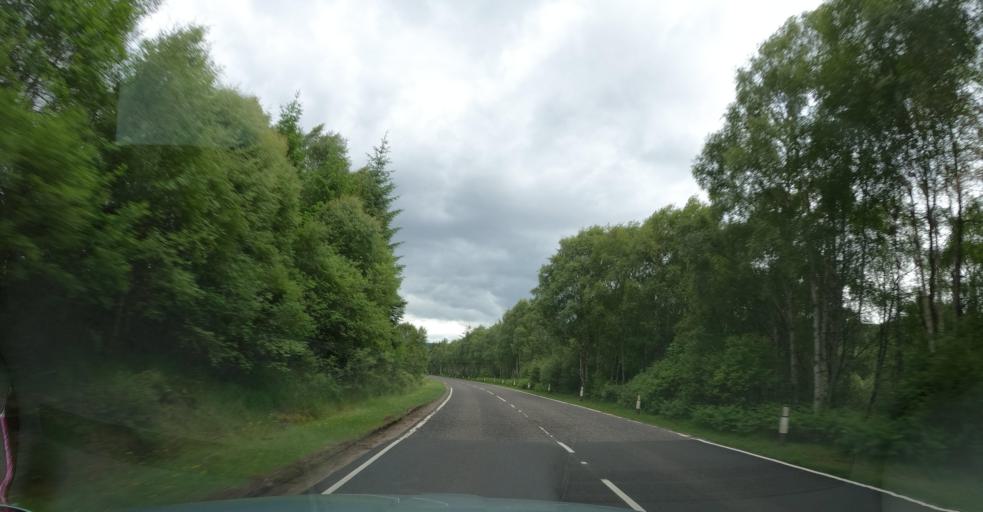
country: GB
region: Scotland
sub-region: Highland
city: Dingwall
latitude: 57.6629
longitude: -4.6733
